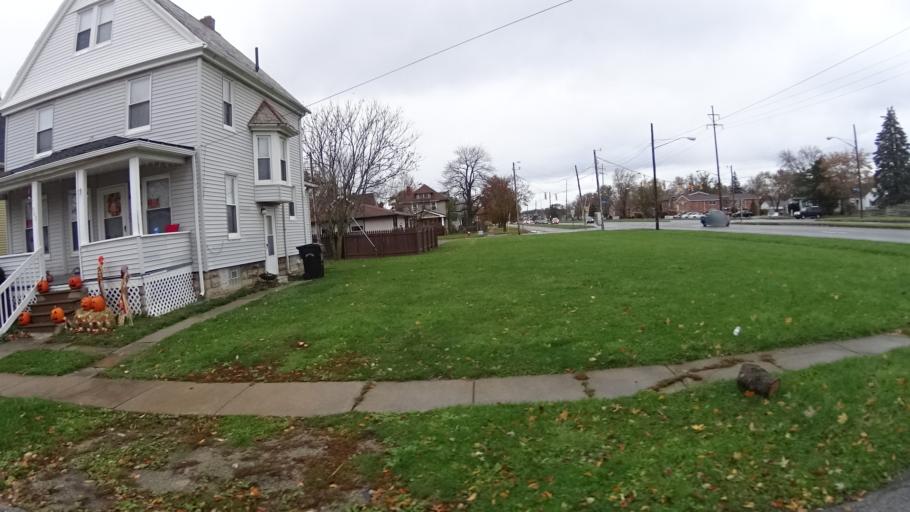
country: US
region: Ohio
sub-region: Lorain County
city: Elyria
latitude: 41.3778
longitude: -82.1174
